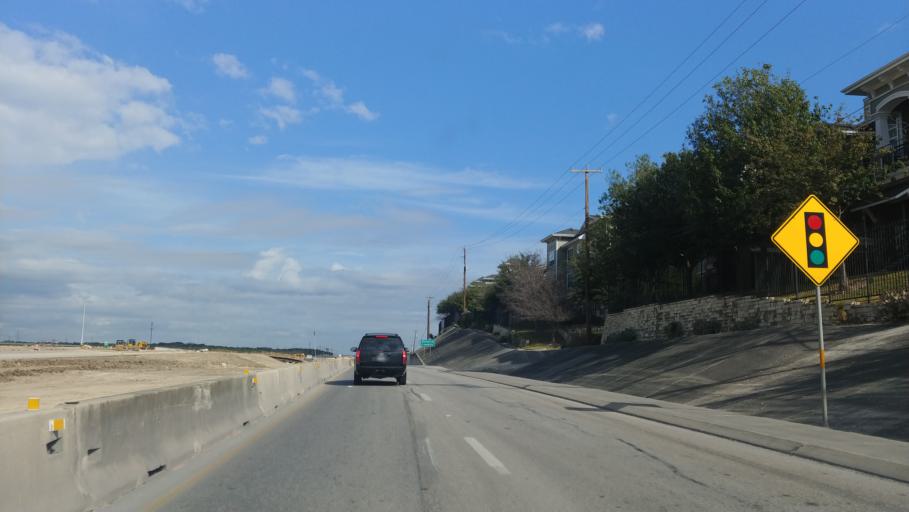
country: US
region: Texas
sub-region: Bexar County
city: Leon Valley
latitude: 29.4624
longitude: -98.7109
